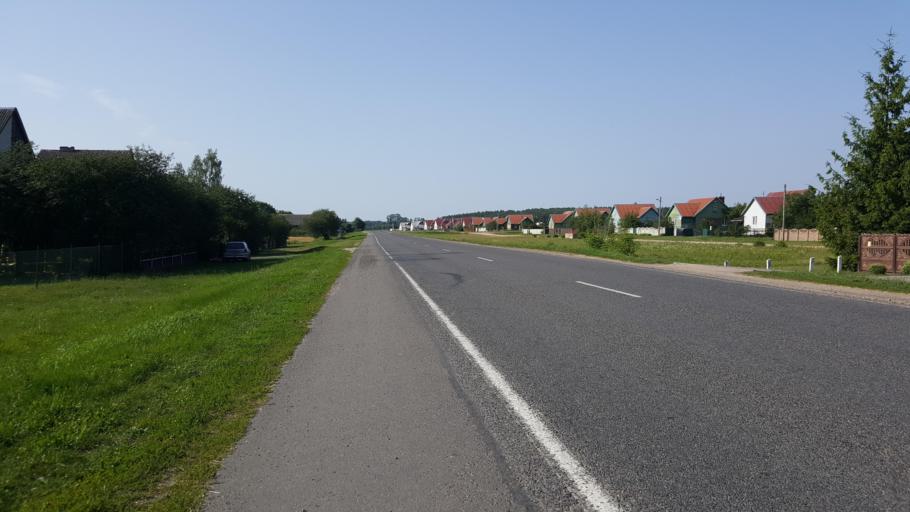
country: BY
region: Brest
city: Kamyanyets
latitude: 52.3236
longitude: 23.9177
